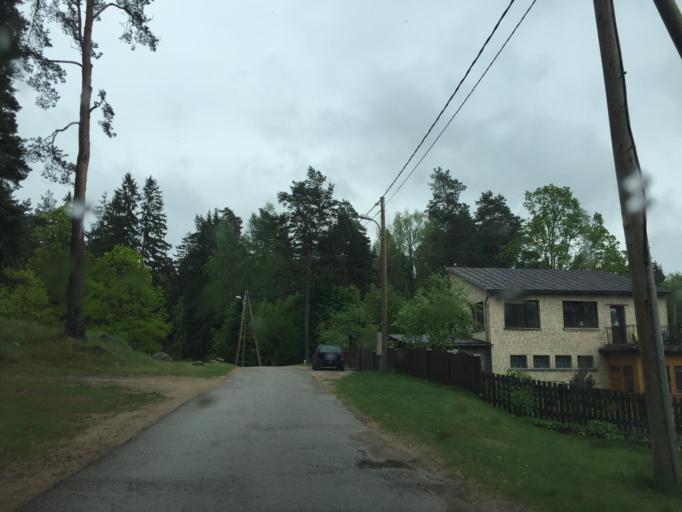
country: LV
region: Kegums
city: Kegums
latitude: 56.7414
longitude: 24.7315
